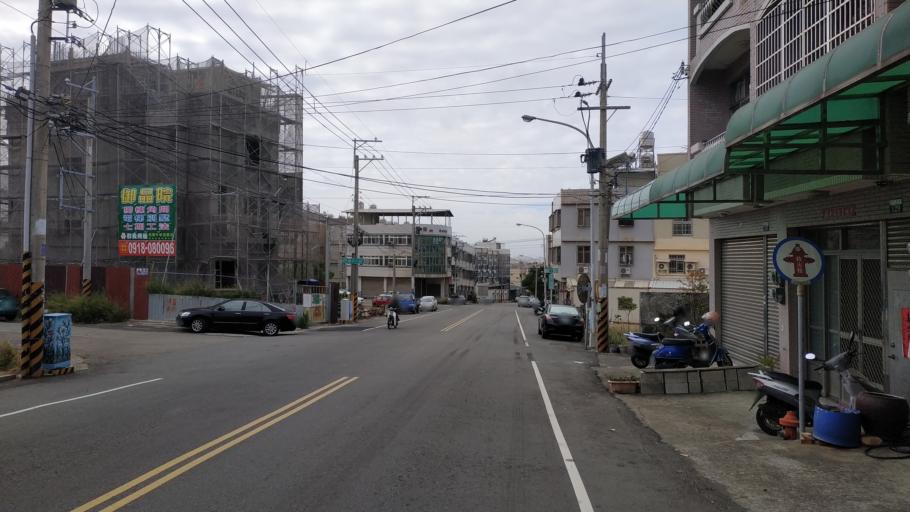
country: TW
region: Taiwan
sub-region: Taichung City
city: Taichung
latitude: 24.2187
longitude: 120.5763
